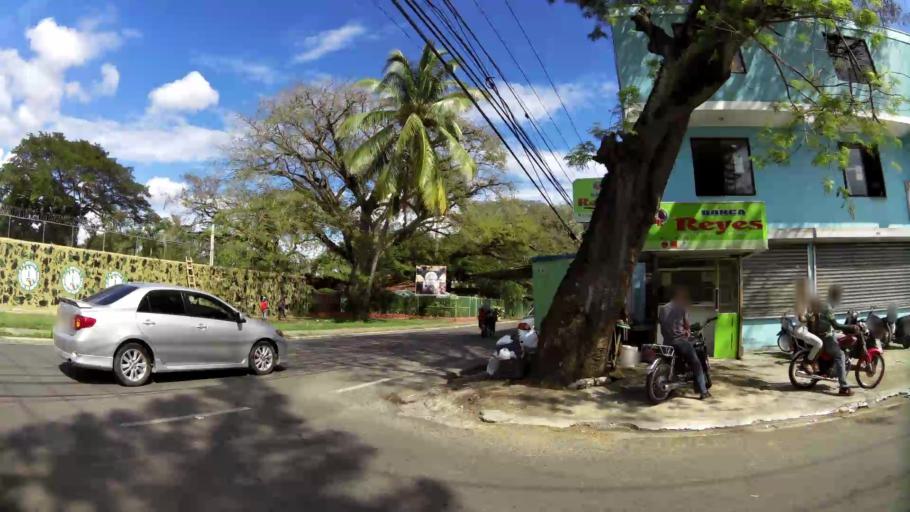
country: DO
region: La Vega
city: Concepcion de La Vega
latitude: 19.2186
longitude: -70.5184
